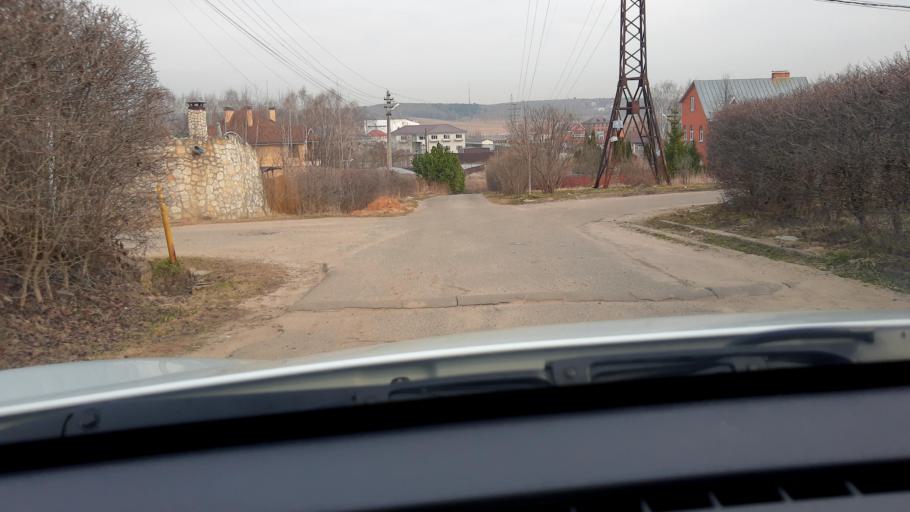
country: RU
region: Moskovskaya
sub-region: Leninskiy Rayon
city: Molokovo
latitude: 55.4920
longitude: 37.8526
